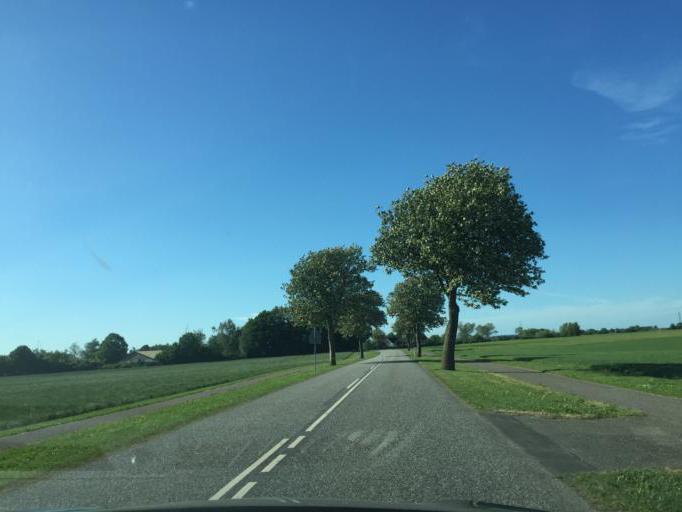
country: DK
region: Zealand
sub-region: Koge Kommune
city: Borup
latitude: 55.4378
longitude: 11.9697
